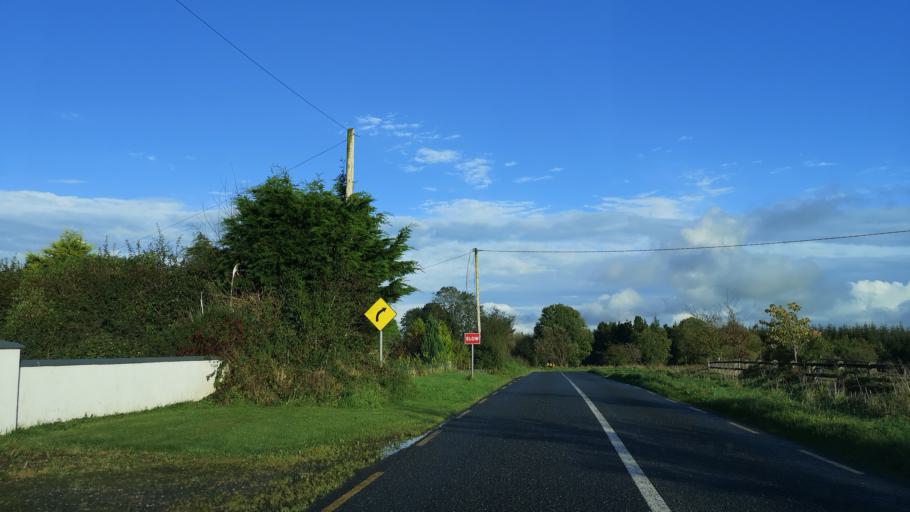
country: IE
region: Connaught
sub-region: Roscommon
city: Castlerea
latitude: 53.8062
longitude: -8.5082
